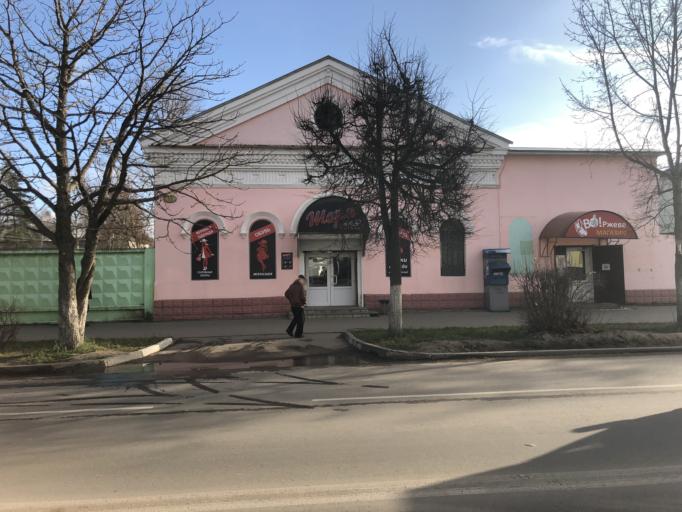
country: RU
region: Tverskaya
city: Rzhev
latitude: 56.2531
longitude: 34.3277
